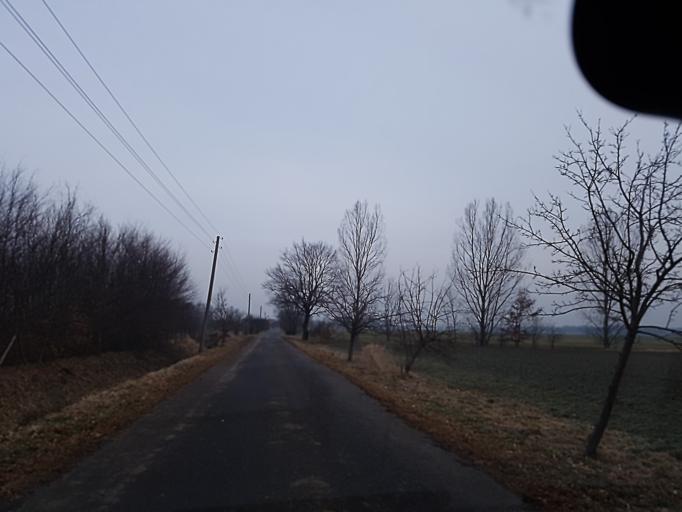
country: DE
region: Brandenburg
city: Ruckersdorf
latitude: 51.5685
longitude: 13.5448
